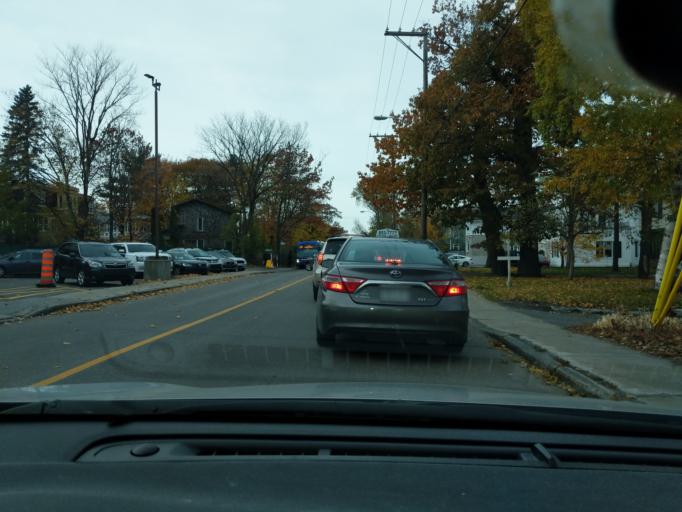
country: CA
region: Quebec
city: Quebec
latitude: 46.7865
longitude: -71.2469
